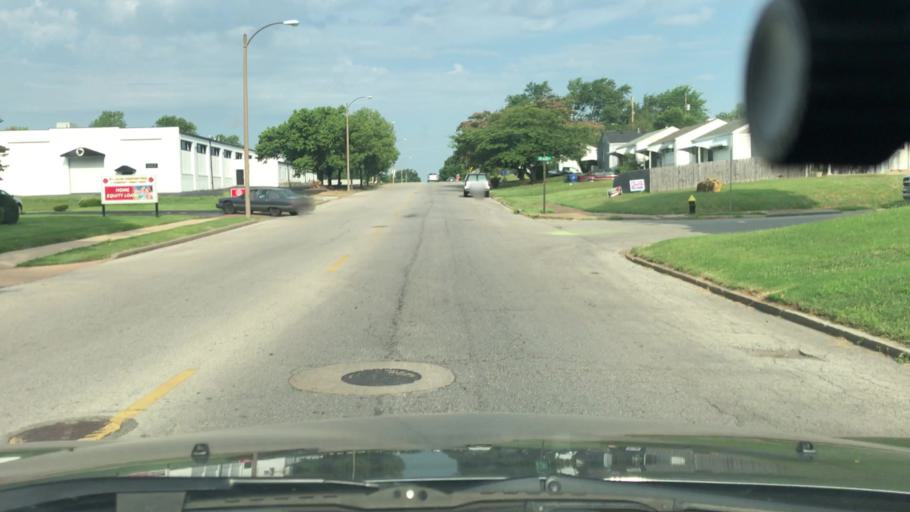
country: US
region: Missouri
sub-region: Saint Louis County
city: Maplewood
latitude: 38.6010
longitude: -90.2820
